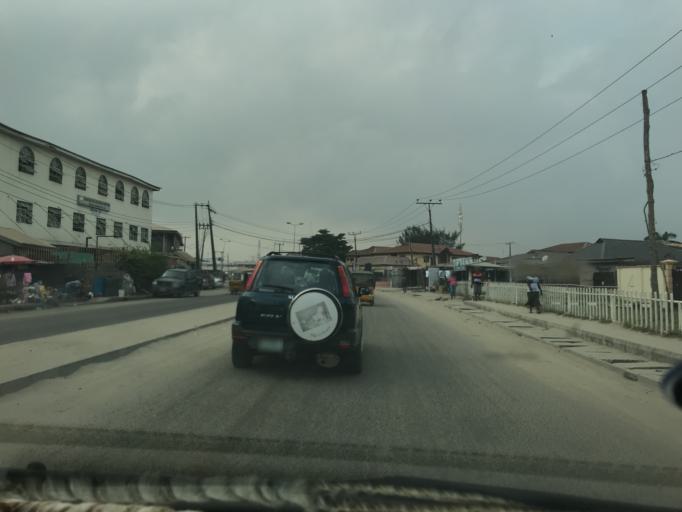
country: NG
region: Lagos
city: Ikoyi
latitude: 6.4726
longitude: 3.5661
